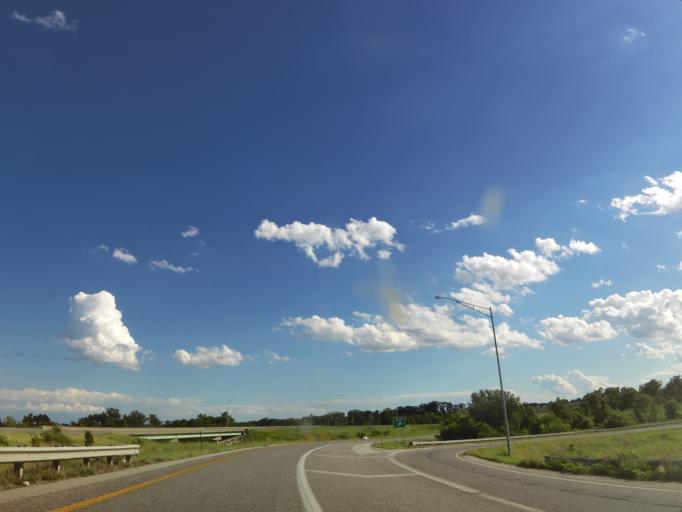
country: US
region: Illinois
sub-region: Adams County
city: Quincy
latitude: 39.9366
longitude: -91.5179
